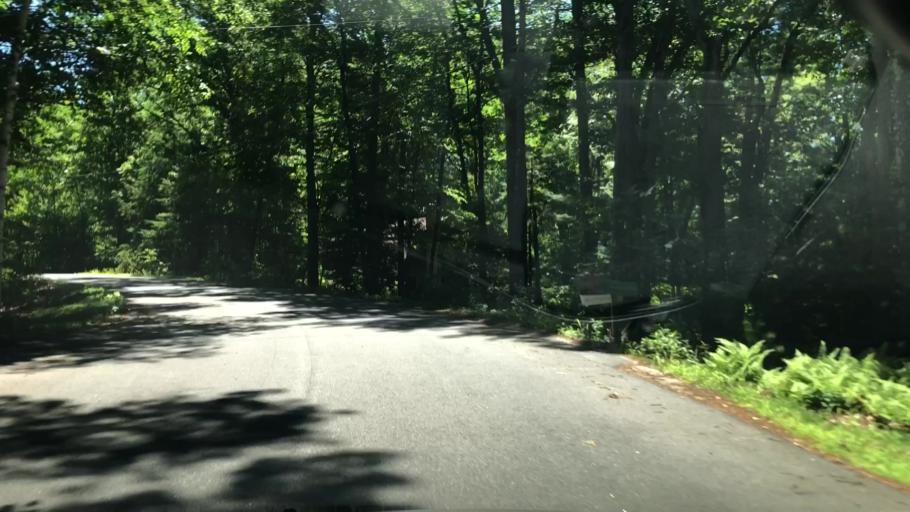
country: US
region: New Hampshire
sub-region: Hillsborough County
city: Milford
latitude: 42.8357
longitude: -71.5793
